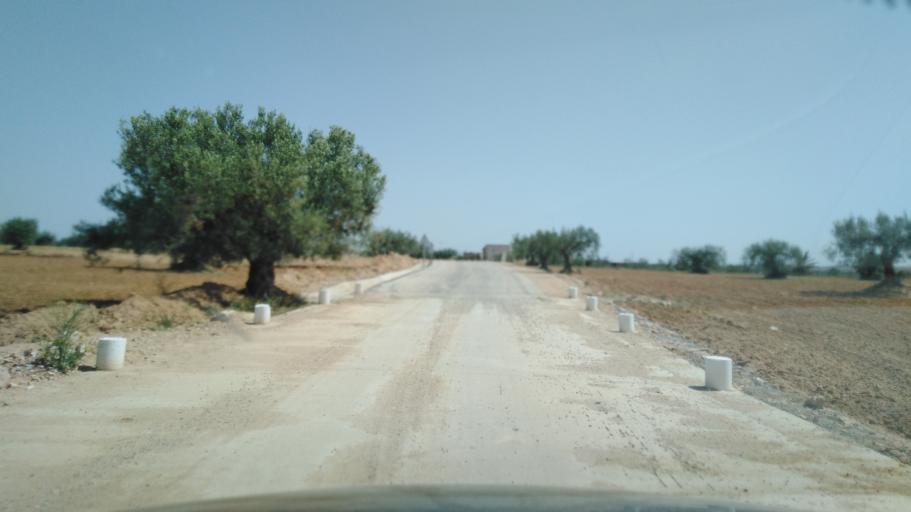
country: TN
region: Safaqis
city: Sfax
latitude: 34.6900
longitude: 10.4492
